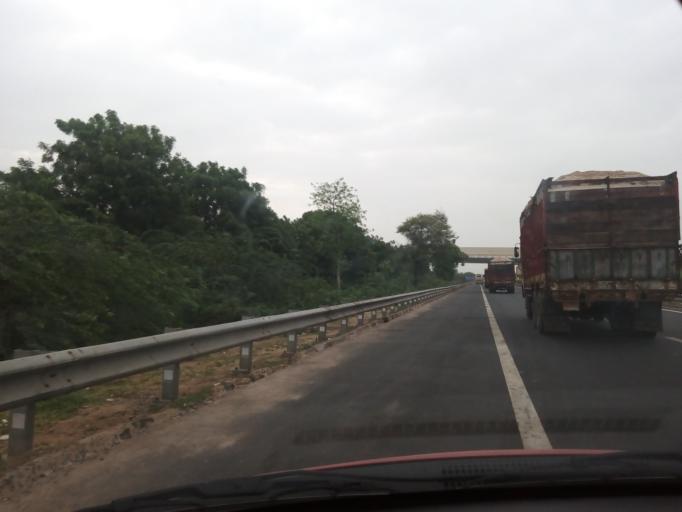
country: IN
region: Gujarat
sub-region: Ahmadabad
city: Ahmedabad
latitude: 22.9740
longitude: 72.6537
